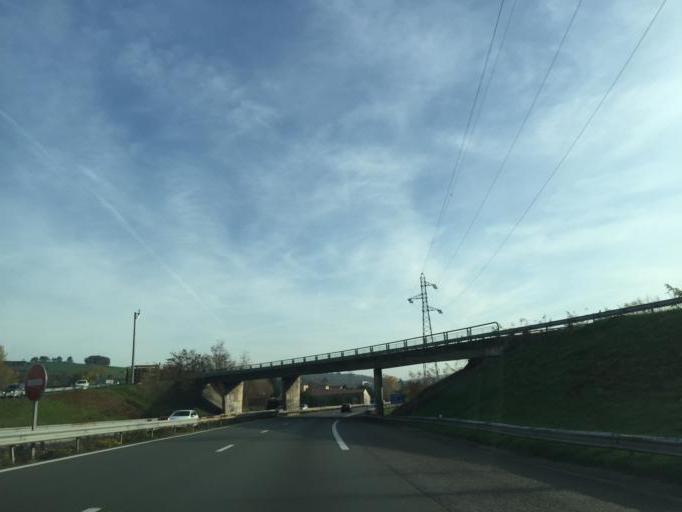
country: FR
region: Rhone-Alpes
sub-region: Departement de la Loire
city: Chateauneuf
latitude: 45.5402
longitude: 4.6428
